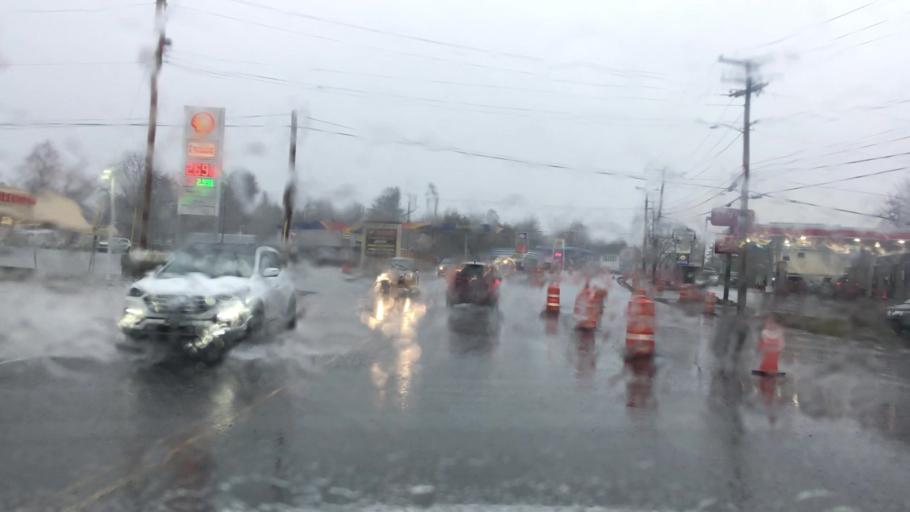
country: US
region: New Hampshire
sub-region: Rockingham County
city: Derry
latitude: 42.8730
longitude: -71.3375
